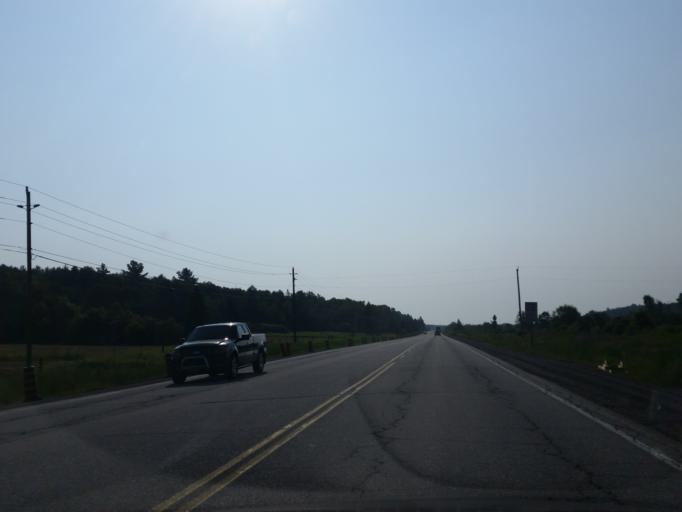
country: CA
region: Ontario
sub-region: Nipissing District
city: North Bay
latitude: 46.4283
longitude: -80.2091
